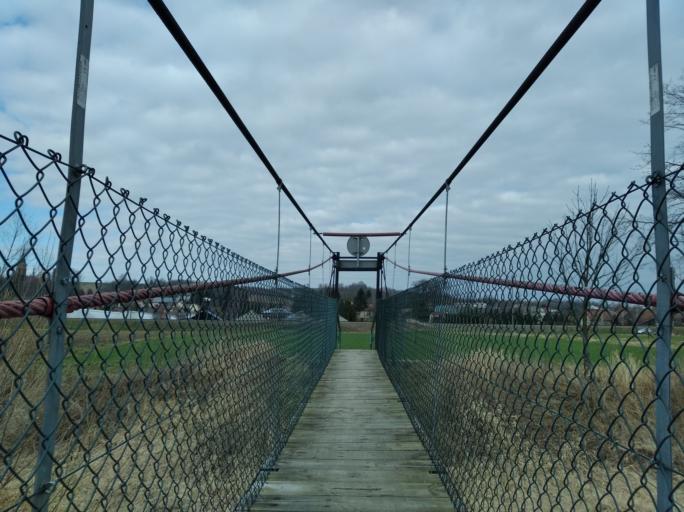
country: PL
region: Subcarpathian Voivodeship
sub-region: Powiat strzyzowski
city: Wysoka Strzyzowska
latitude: 49.8737
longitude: 21.7222
